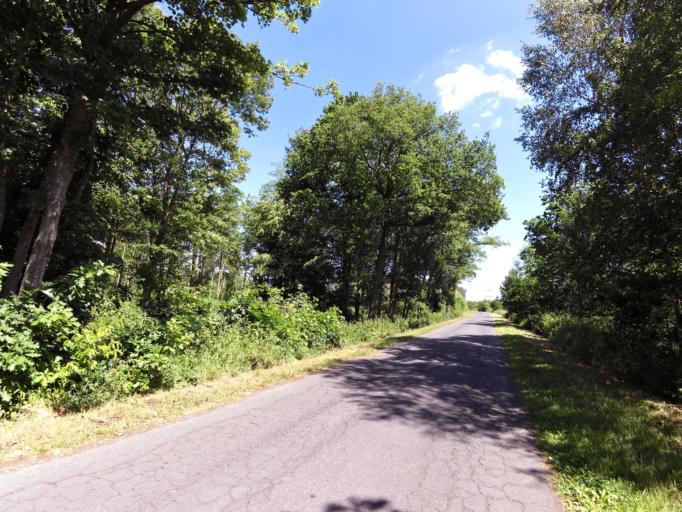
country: BE
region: Flanders
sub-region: Provincie West-Vlaanderen
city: Zedelgem
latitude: 51.1463
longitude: 3.1140
